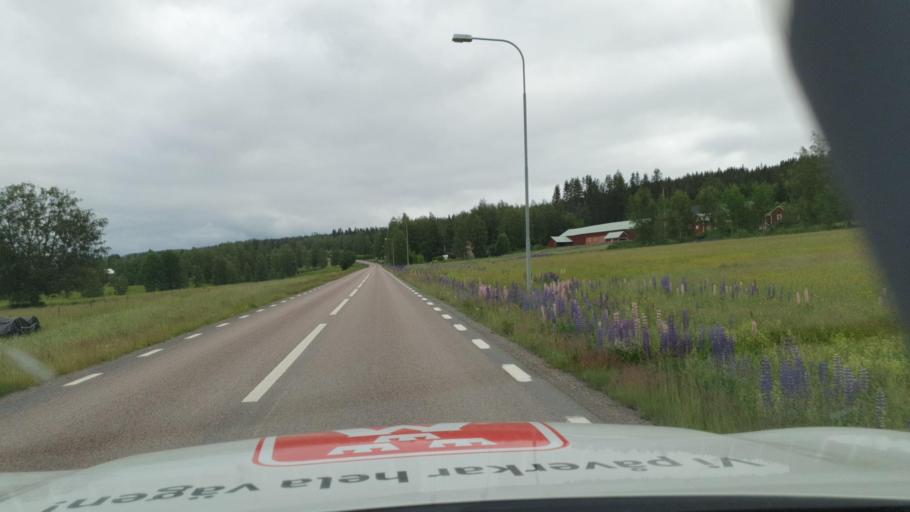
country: SE
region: Vaermland
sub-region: Sunne Kommun
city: Sunne
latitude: 59.8476
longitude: 12.9455
